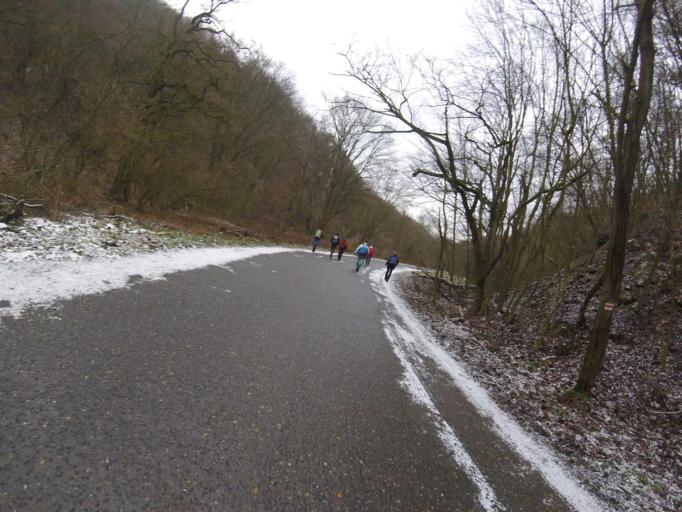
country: HU
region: Pest
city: Visegrad
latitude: 47.7589
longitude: 18.9809
